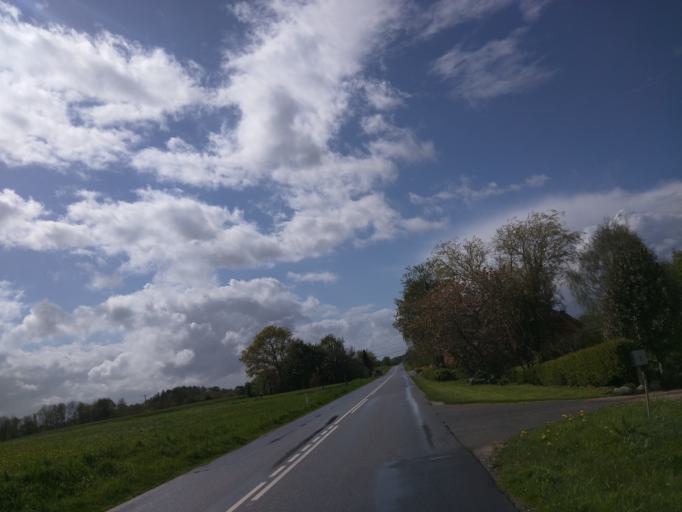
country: DK
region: Central Jutland
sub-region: Silkeborg Kommune
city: Kjellerup
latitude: 56.2773
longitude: 9.5027
